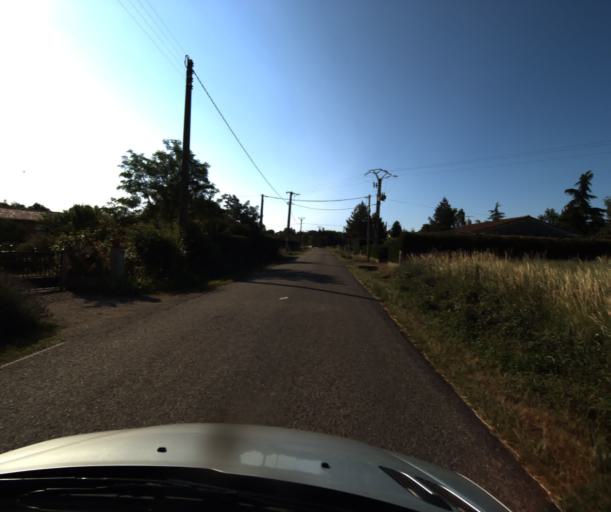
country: FR
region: Midi-Pyrenees
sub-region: Departement du Tarn-et-Garonne
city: Saint-Porquier
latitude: 44.0720
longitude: 1.1972
